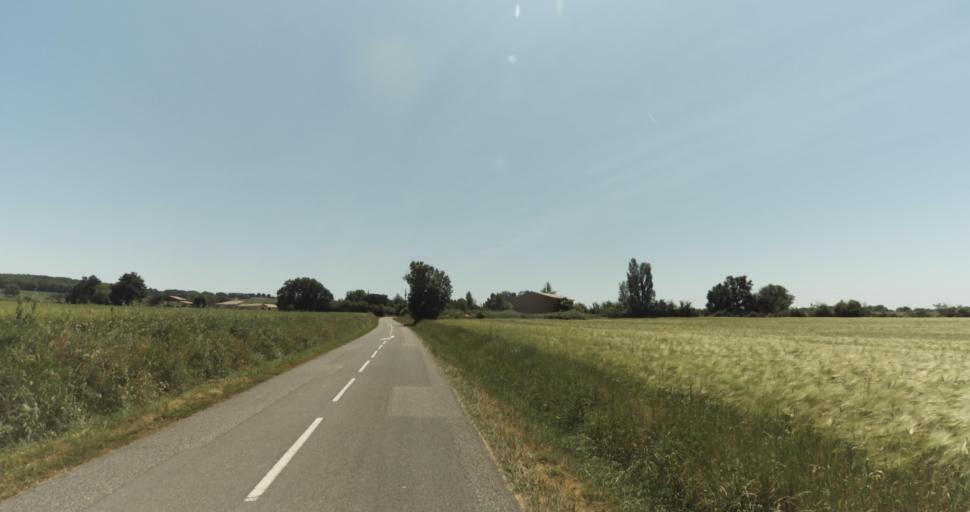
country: FR
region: Midi-Pyrenees
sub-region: Departement de la Haute-Garonne
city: Levignac
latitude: 43.6501
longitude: 1.1757
